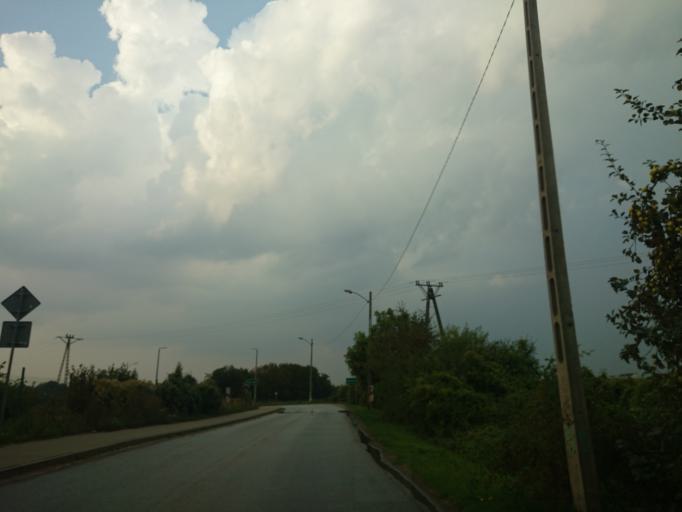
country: PL
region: West Pomeranian Voivodeship
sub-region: Powiat policki
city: Przeclaw
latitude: 53.3796
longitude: 14.4686
